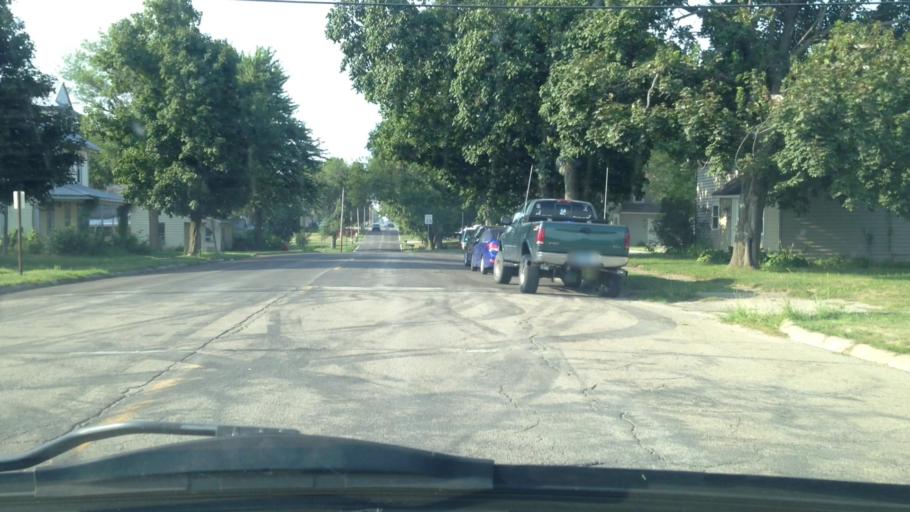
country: US
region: Iowa
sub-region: Henry County
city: Winfield
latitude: 41.2144
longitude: -91.5388
